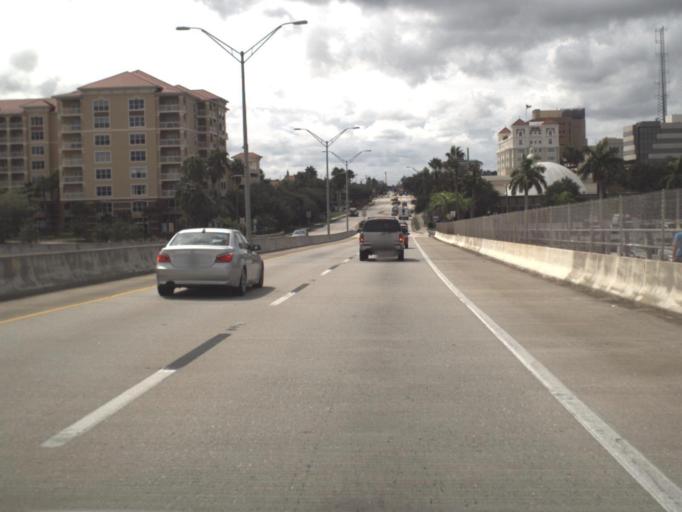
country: US
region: Florida
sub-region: Manatee County
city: Bradenton
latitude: 27.5006
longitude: -82.5712
